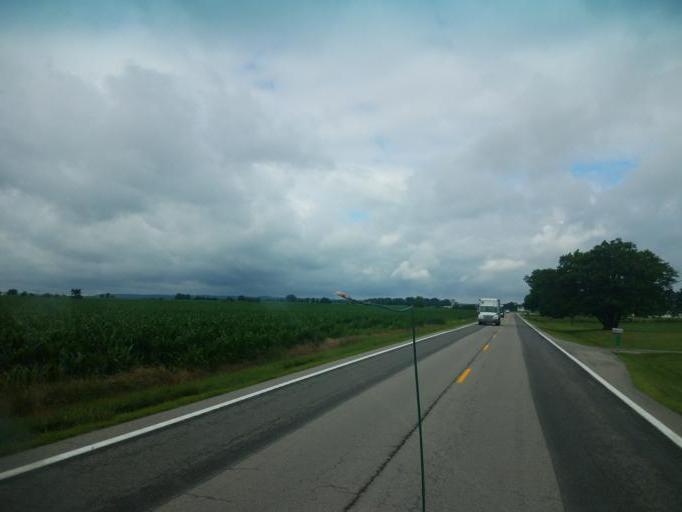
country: US
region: Ohio
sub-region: Champaign County
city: North Lewisburg
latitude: 40.4062
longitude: -83.5546
